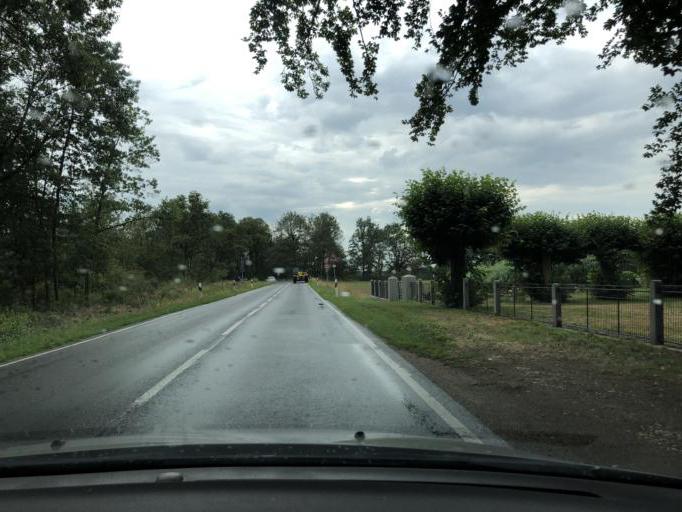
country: DE
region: North Rhine-Westphalia
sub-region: Regierungsbezirk Dusseldorf
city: Schermbeck
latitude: 51.6357
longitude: 6.8963
